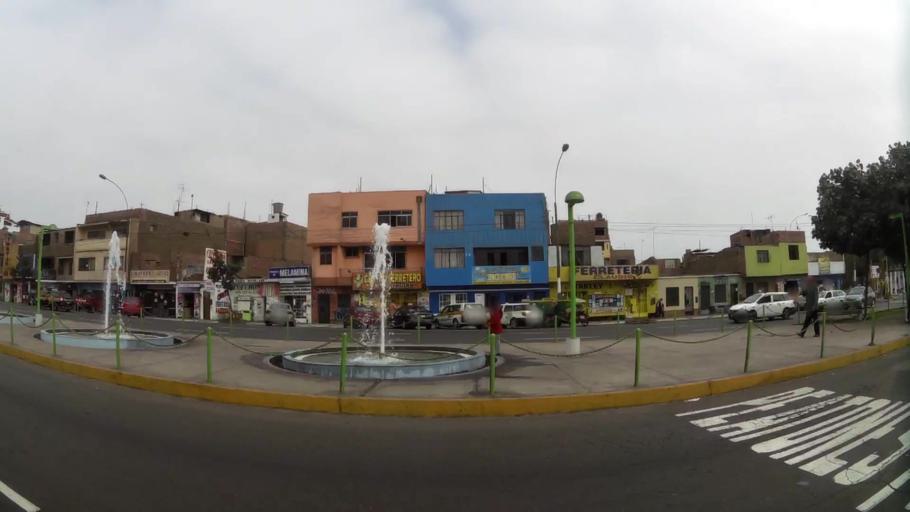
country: PE
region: Callao
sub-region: Callao
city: Callao
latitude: -12.0313
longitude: -77.0836
